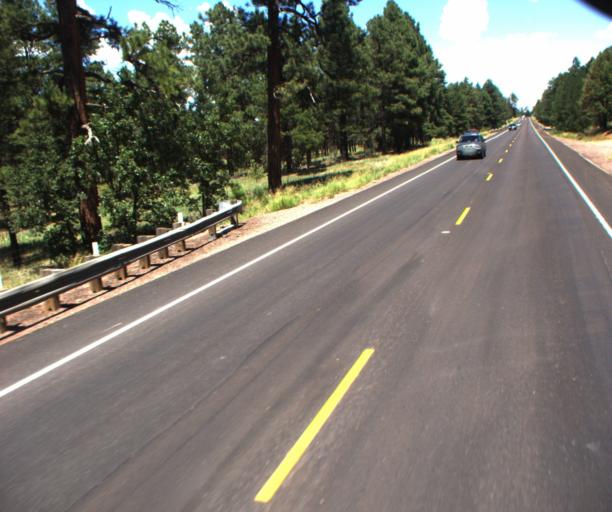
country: US
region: Arizona
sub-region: Navajo County
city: Show Low
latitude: 34.2225
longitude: -110.0711
